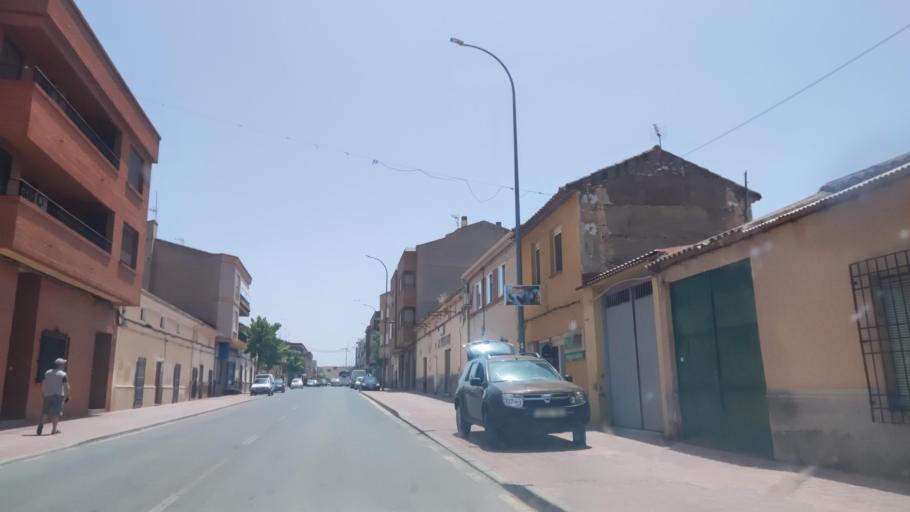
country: ES
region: Castille-La Mancha
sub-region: Provincia de Albacete
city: Pozo-Canada
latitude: 38.8050
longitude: -1.7336
